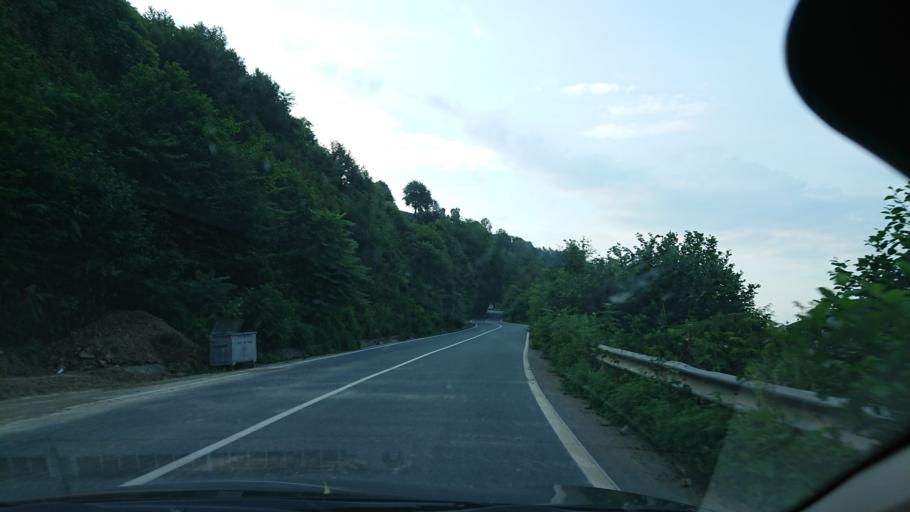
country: TR
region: Rize
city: Cayeli
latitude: 41.0702
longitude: 40.7119
